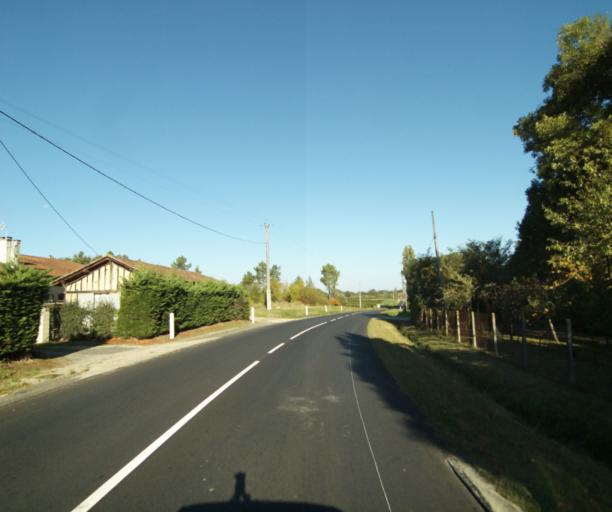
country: FR
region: Midi-Pyrenees
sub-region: Departement du Gers
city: Cazaubon
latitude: 43.8920
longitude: -0.0077
